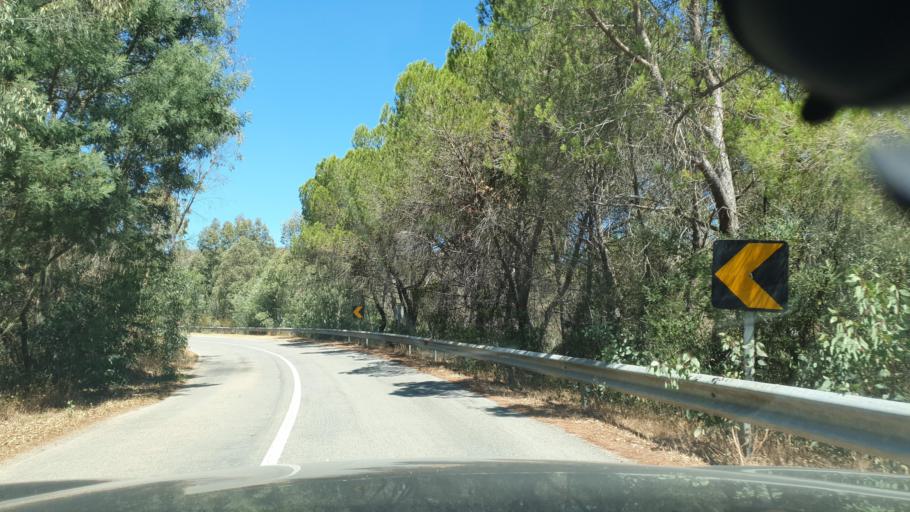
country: PT
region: Beja
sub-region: Odemira
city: Odemira
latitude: 37.5098
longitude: -8.4617
